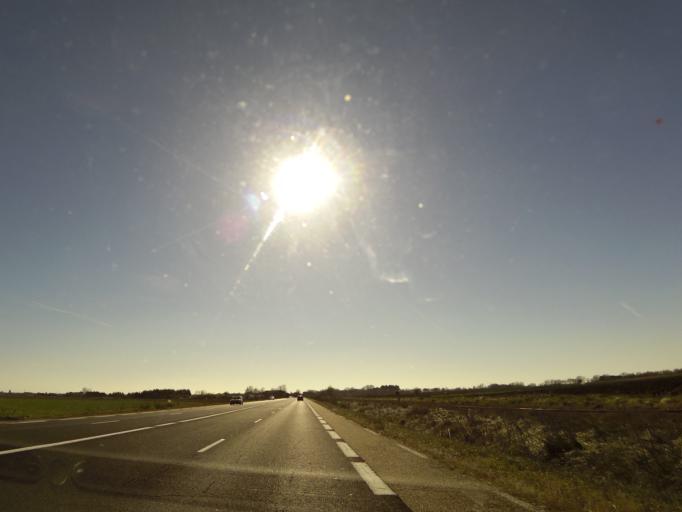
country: FR
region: Languedoc-Roussillon
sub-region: Departement de l'Herault
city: Marsillargues
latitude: 43.6528
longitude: 4.2007
